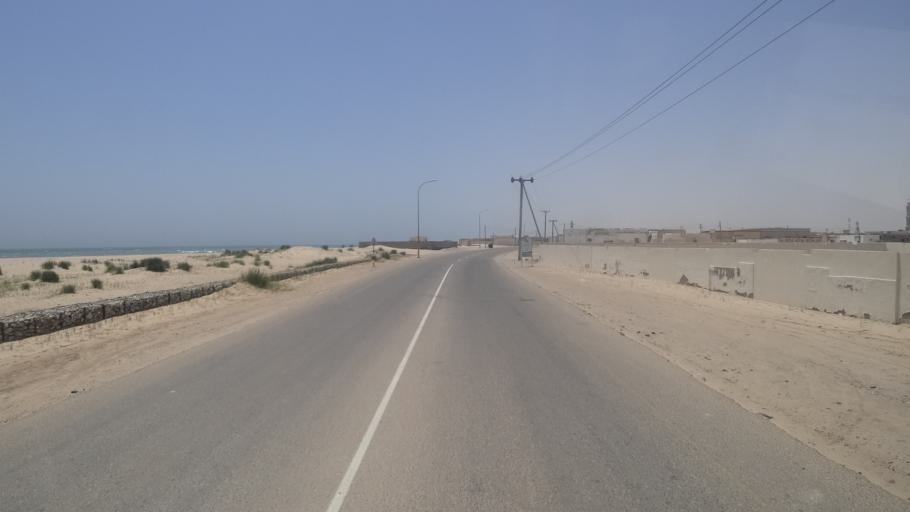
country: OM
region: Ash Sharqiyah
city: Sur
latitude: 22.0887
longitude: 59.6895
